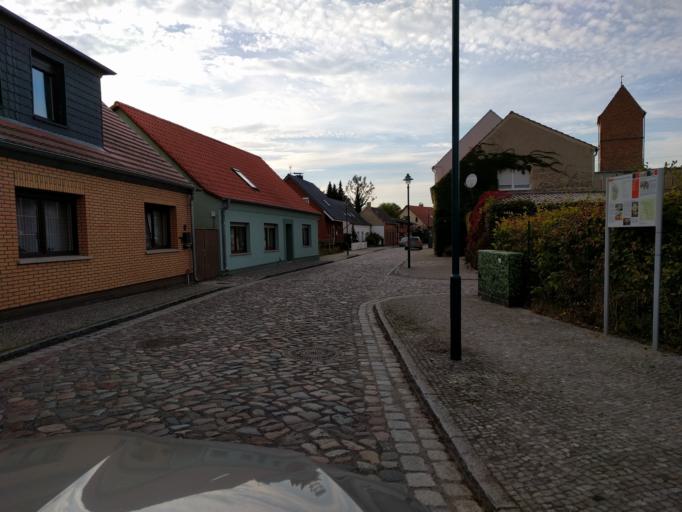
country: DE
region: Brandenburg
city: Ziesar
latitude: 52.2628
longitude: 12.2904
